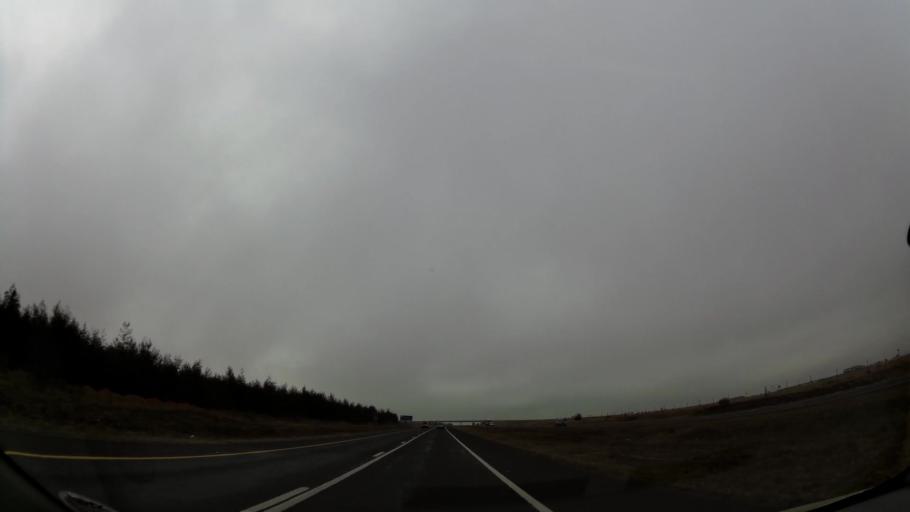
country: ZA
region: Mpumalanga
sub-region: Nkangala District Municipality
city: Delmas
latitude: -26.0709
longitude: 28.7512
